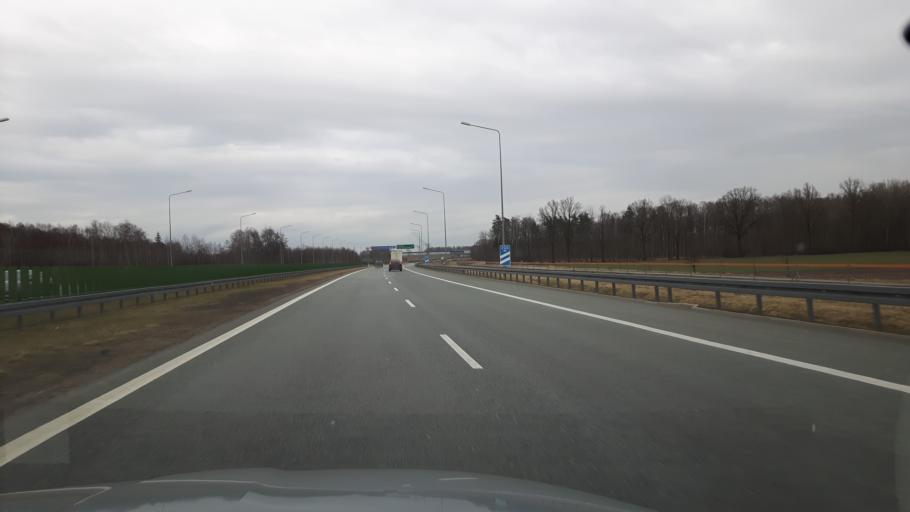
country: PL
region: Masovian Voivodeship
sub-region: Powiat minski
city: Jakubow
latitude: 52.2162
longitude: 21.6363
